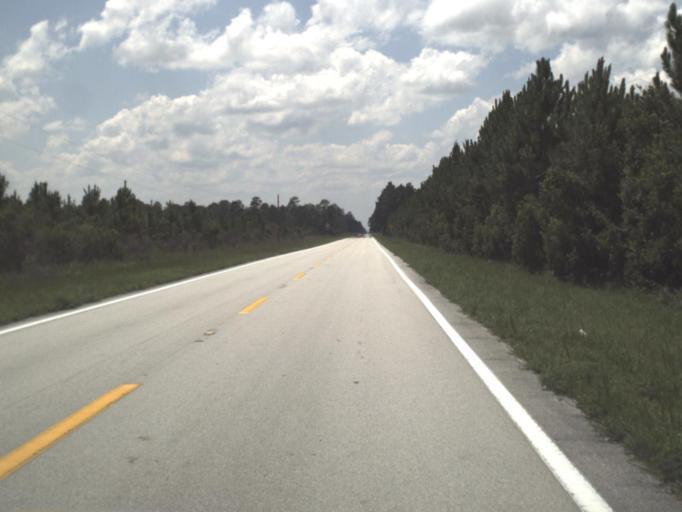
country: US
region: Florida
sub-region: Baker County
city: Macclenny
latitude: 30.5145
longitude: -82.2722
